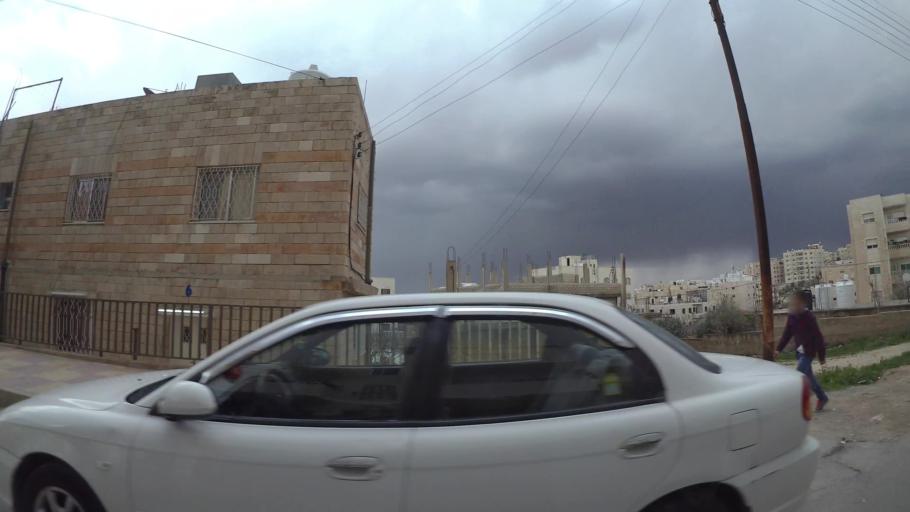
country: JO
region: Amman
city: Amman
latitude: 32.0089
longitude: 35.9490
